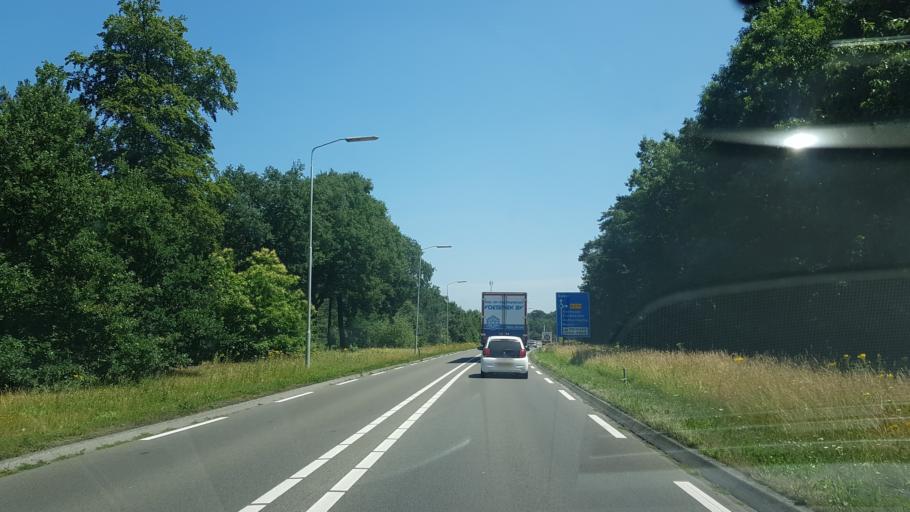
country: NL
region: North Brabant
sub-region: Gemeente Helmond
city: Helmond
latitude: 51.4881
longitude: 5.7023
